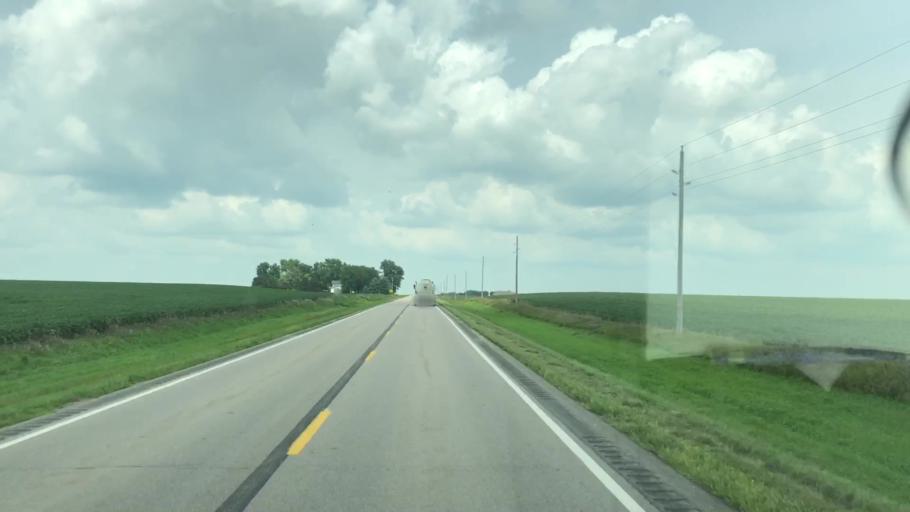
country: US
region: Iowa
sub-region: Plymouth County
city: Remsen
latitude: 42.7867
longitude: -95.9578
